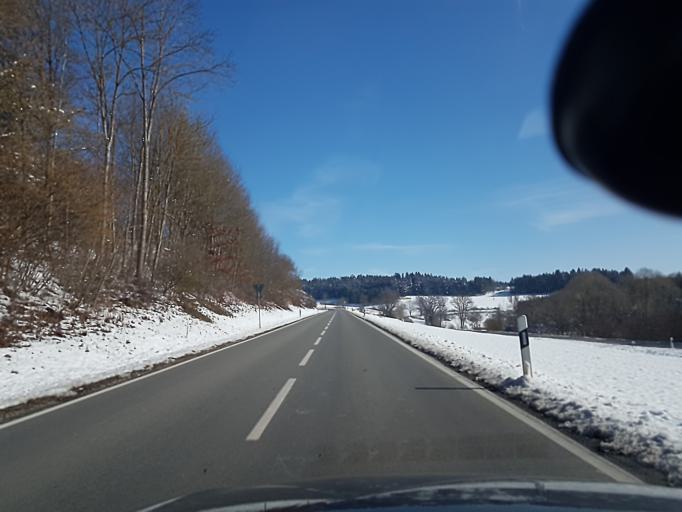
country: DE
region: Baden-Wuerttemberg
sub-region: Freiburg Region
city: Niedereschach
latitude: 48.1664
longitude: 8.5371
